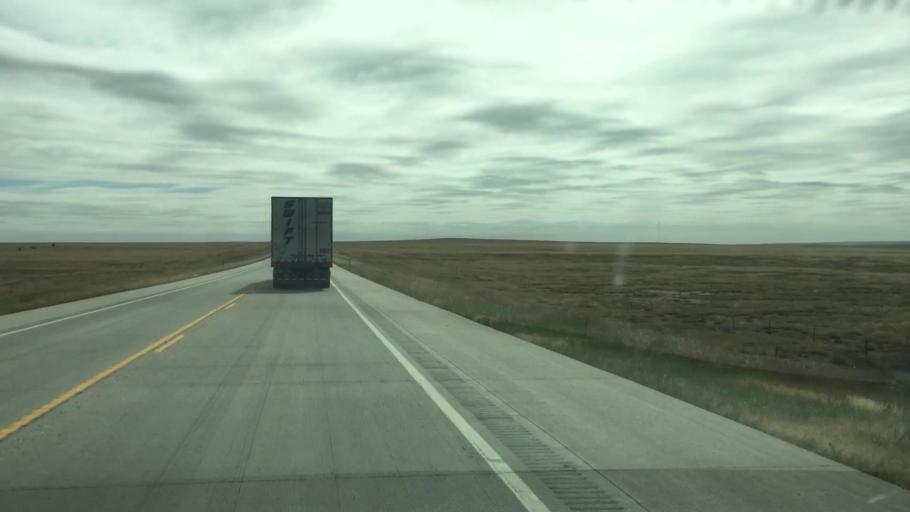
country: US
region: Colorado
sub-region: Lincoln County
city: Hugo
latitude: 38.9715
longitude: -103.2494
